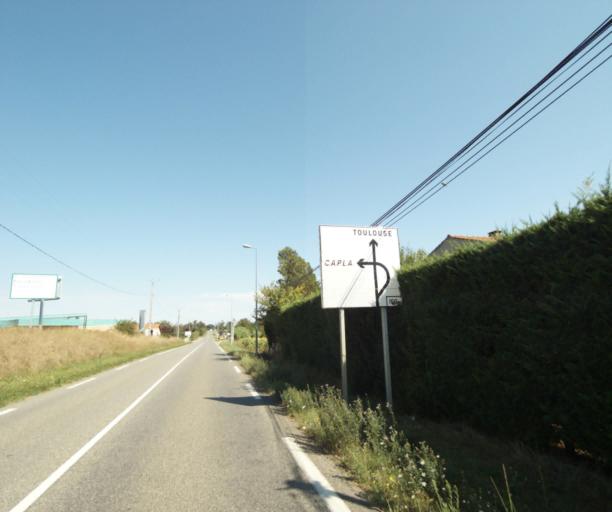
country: FR
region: Midi-Pyrenees
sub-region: Departement de l'Ariege
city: Lezat-sur-Leze
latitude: 43.2892
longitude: 1.3439
